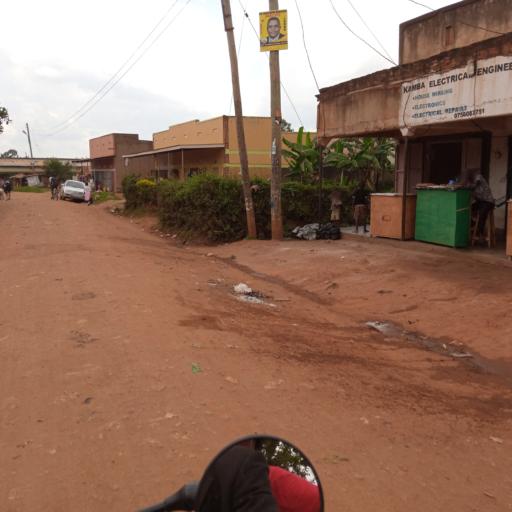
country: UG
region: Eastern Region
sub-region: Mbale District
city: Mbale
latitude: 1.0939
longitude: 34.1720
